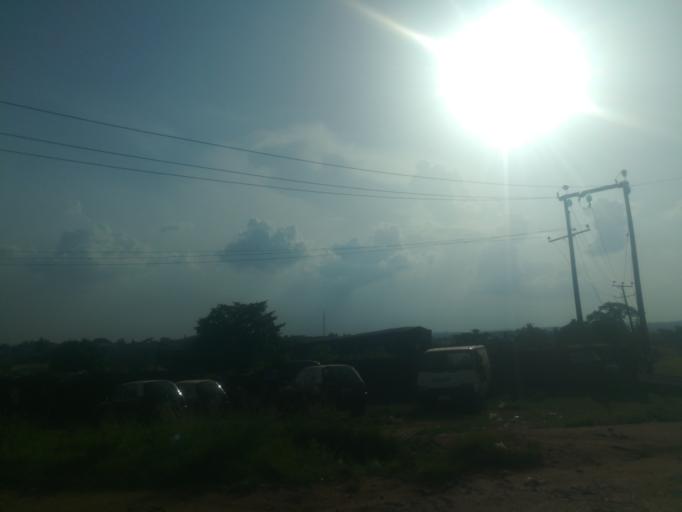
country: NG
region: Oyo
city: Moniya
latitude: 7.5181
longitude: 3.9142
